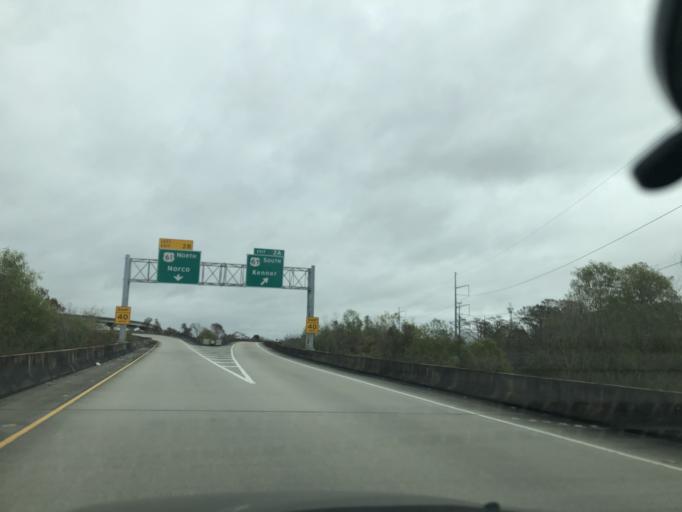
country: US
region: Louisiana
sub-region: Saint Charles Parish
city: Saint Rose
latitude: 29.9725
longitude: -90.3218
